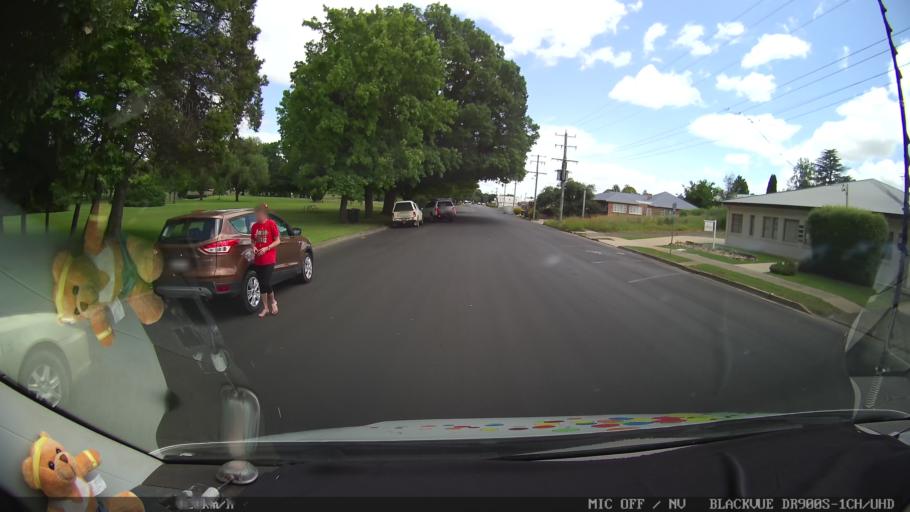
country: AU
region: New South Wales
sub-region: Glen Innes Severn
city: Glen Innes
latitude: -29.7378
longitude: 151.7339
